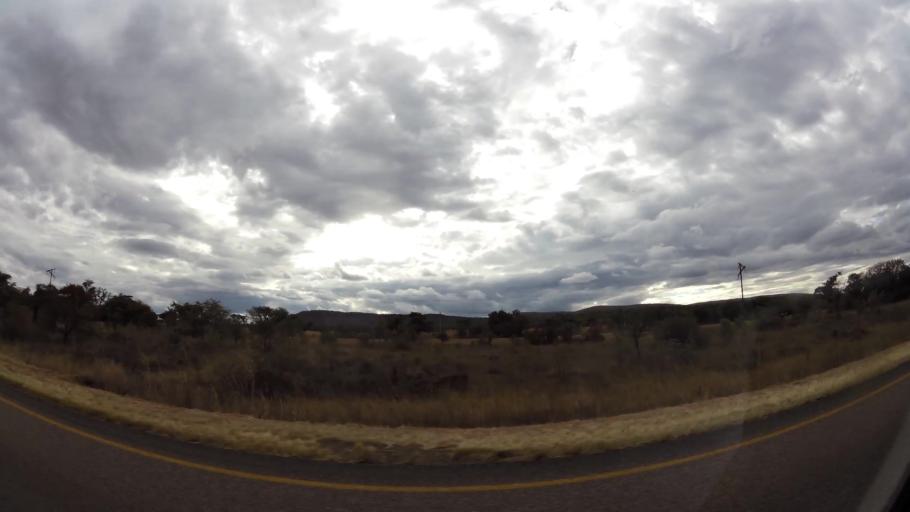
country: ZA
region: Limpopo
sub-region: Waterberg District Municipality
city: Modimolle
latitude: -24.6445
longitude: 28.5953
